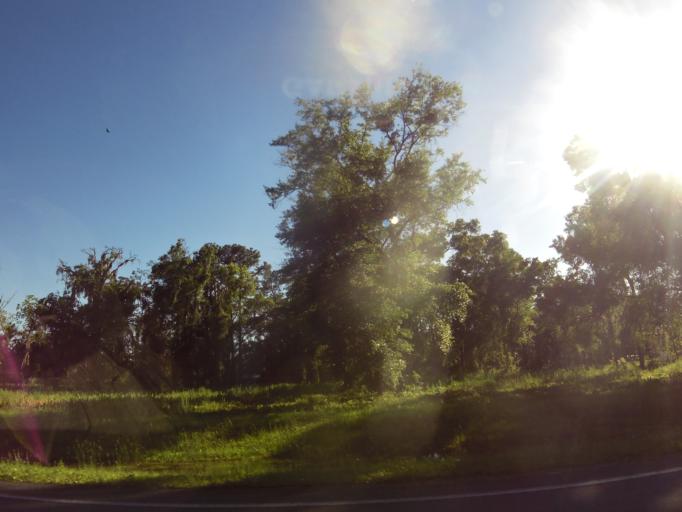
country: US
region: Florida
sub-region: Bradford County
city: Starke
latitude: 29.9314
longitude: -82.1151
